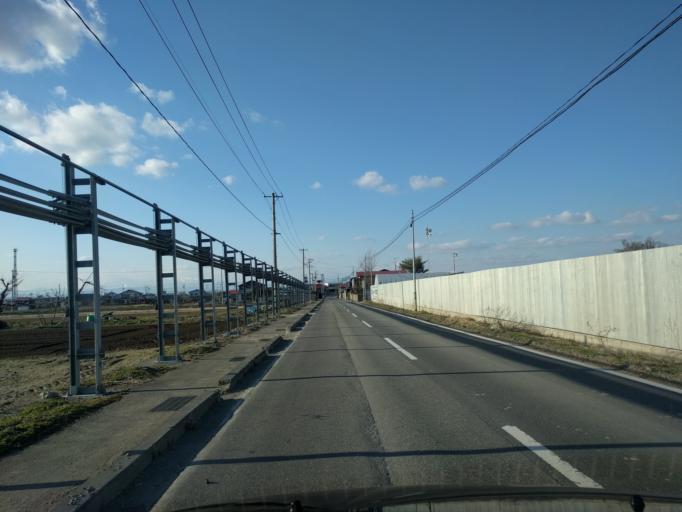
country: JP
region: Fukushima
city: Kitakata
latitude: 37.4710
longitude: 139.8962
